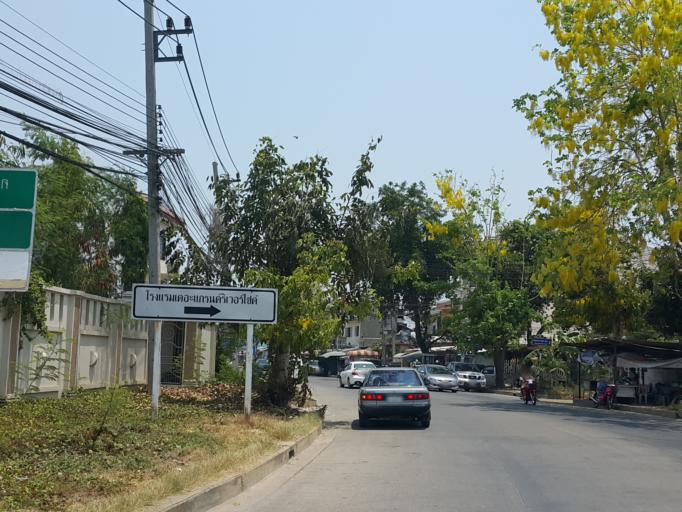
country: TH
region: Phitsanulok
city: Phitsanulok
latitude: 16.8130
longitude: 100.2559
